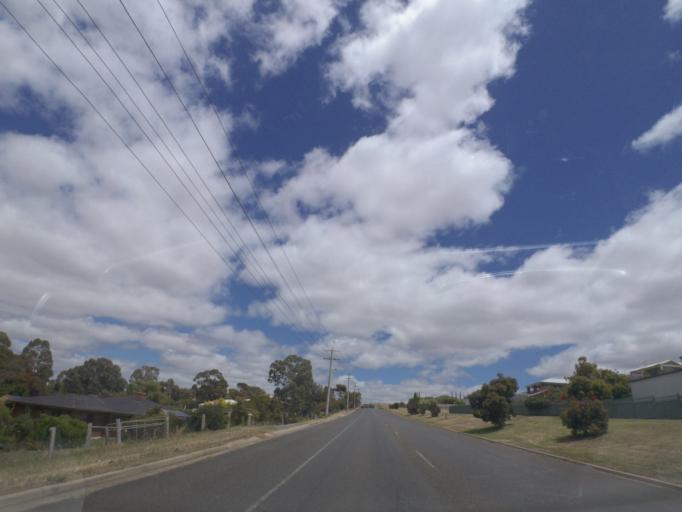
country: AU
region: Victoria
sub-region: Moorabool
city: Bacchus Marsh
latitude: -37.6576
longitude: 144.4280
